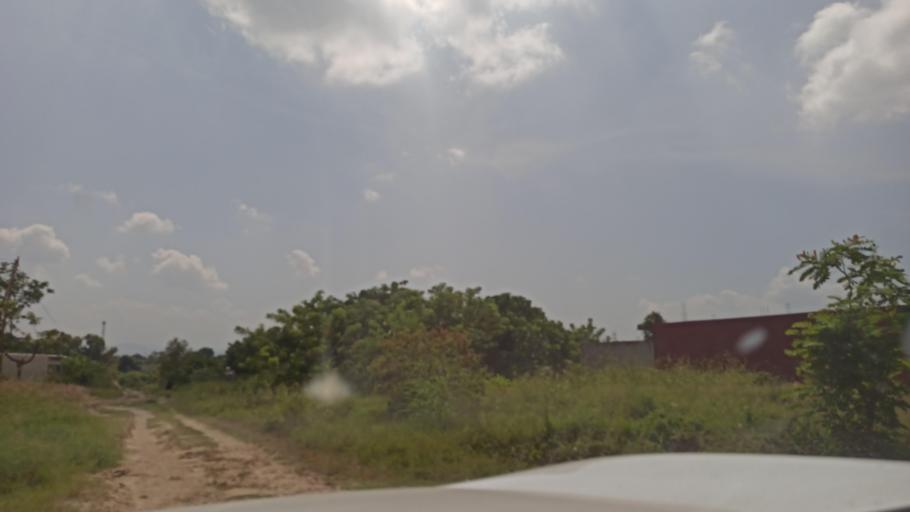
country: MX
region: Veracruz
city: Martinez de la Torre
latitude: 20.0811
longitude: -97.0773
